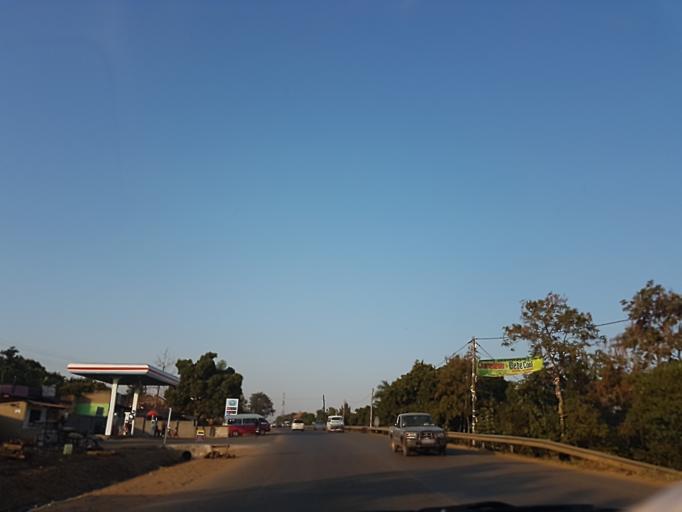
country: UG
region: Central Region
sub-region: Wakiso District
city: Kireka
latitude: 0.4103
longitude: 32.5947
